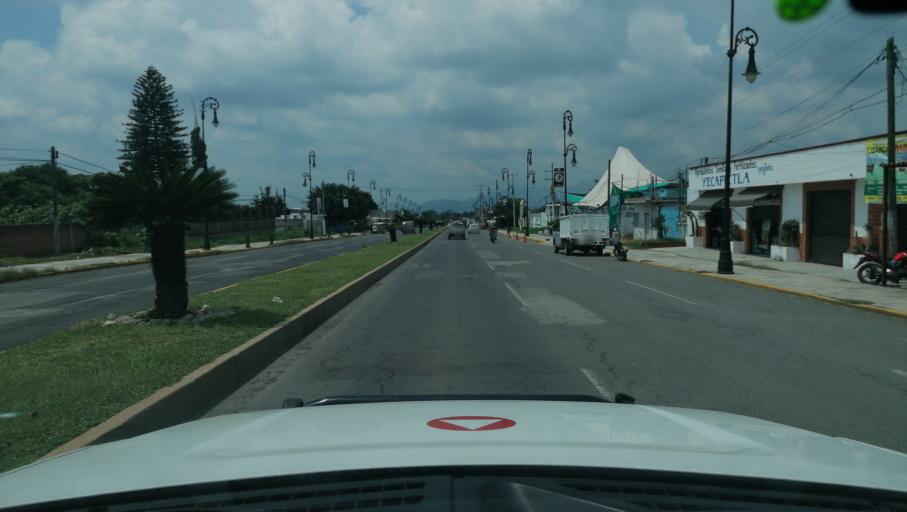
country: MX
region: Morelos
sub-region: Yecapixtla
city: Yecapixtla
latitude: 18.8857
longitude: -98.8714
